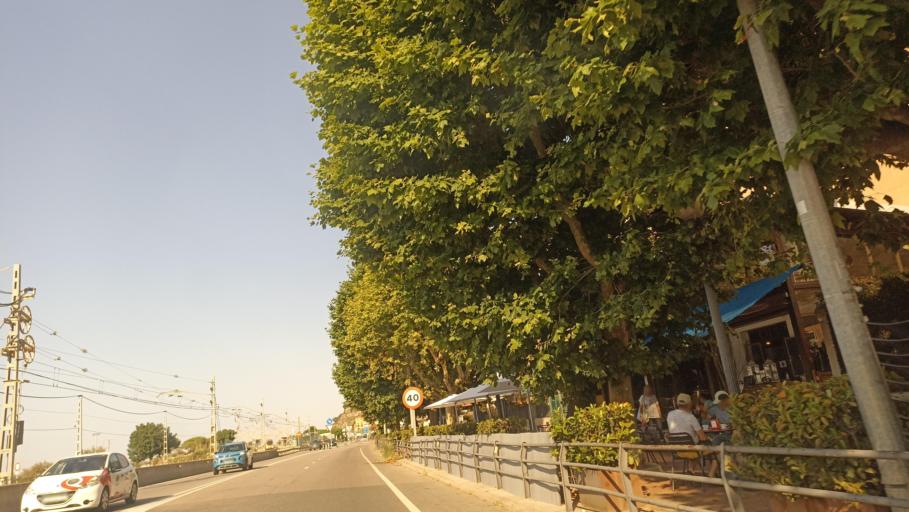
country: ES
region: Catalonia
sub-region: Provincia de Barcelona
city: Arenys de Mar
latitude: 41.5792
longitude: 2.5529
